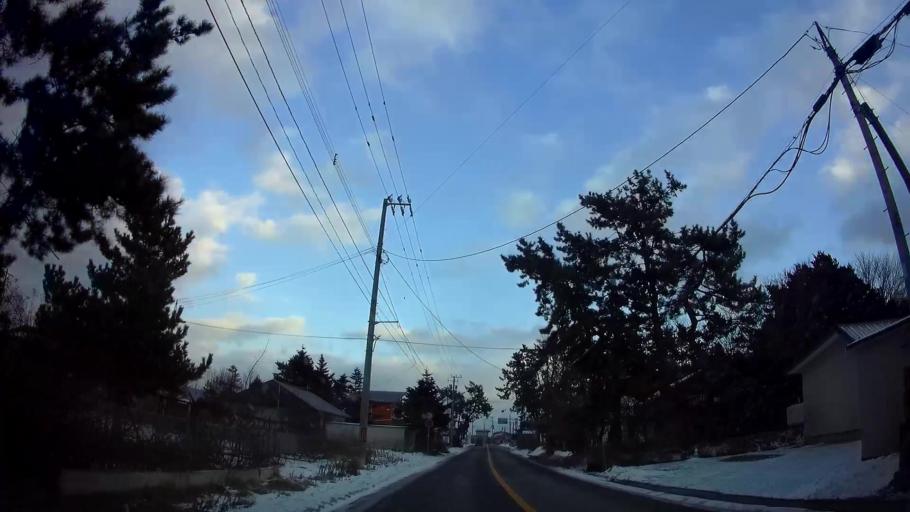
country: JP
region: Hokkaido
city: Nanae
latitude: 42.0294
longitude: 140.8287
